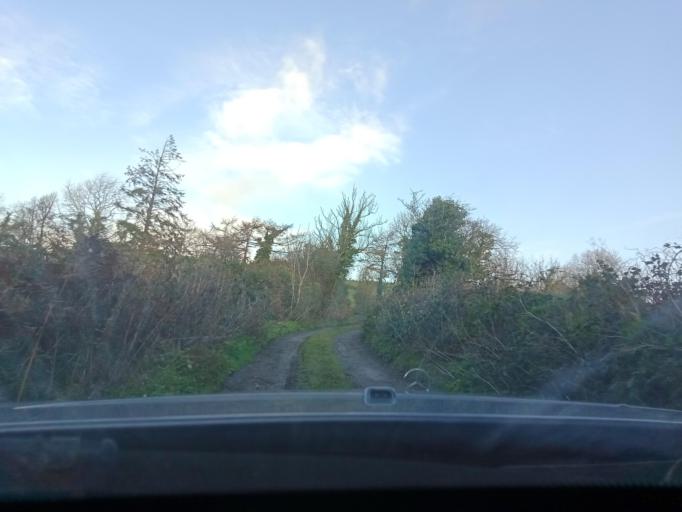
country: IE
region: Leinster
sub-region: Kilkenny
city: Callan
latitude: 52.4604
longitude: -7.4306
